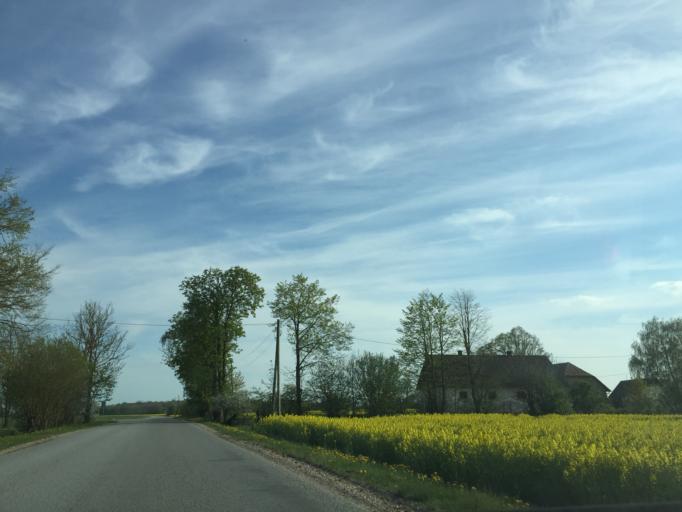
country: LV
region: Bauskas Rajons
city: Bauska
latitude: 56.3921
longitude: 24.2054
